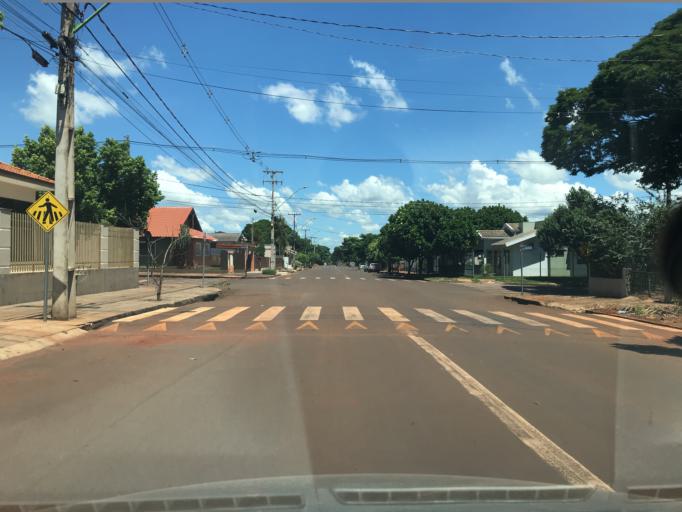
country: BR
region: Parana
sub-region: Palotina
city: Palotina
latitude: -24.2855
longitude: -53.8440
